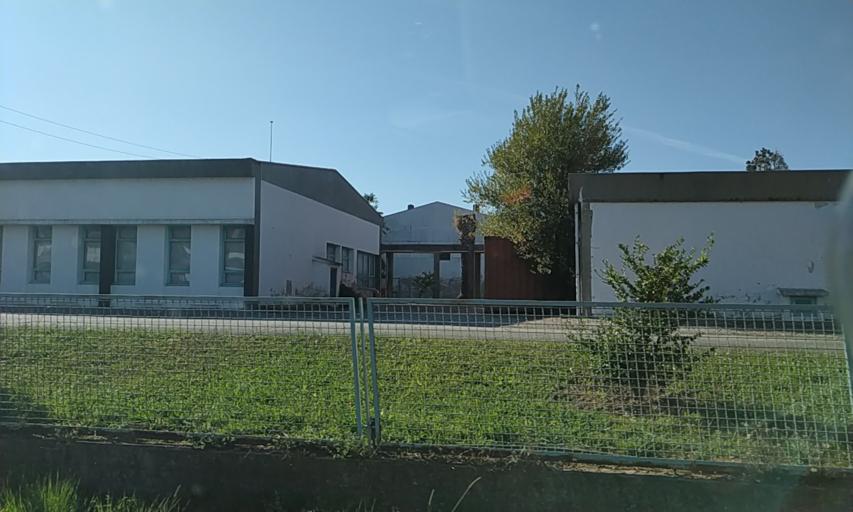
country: PT
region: Porto
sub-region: Pacos de Ferreira
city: Seroa
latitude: 41.2655
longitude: -8.4776
